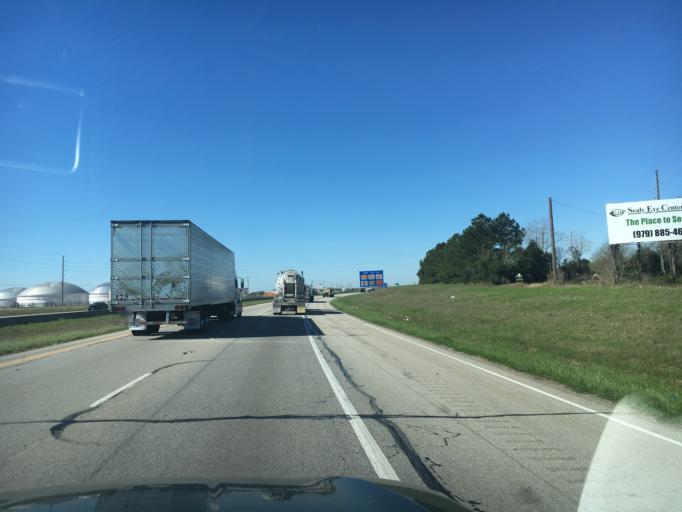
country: US
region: Texas
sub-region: Austin County
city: Sealy
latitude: 29.7688
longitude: -96.1408
